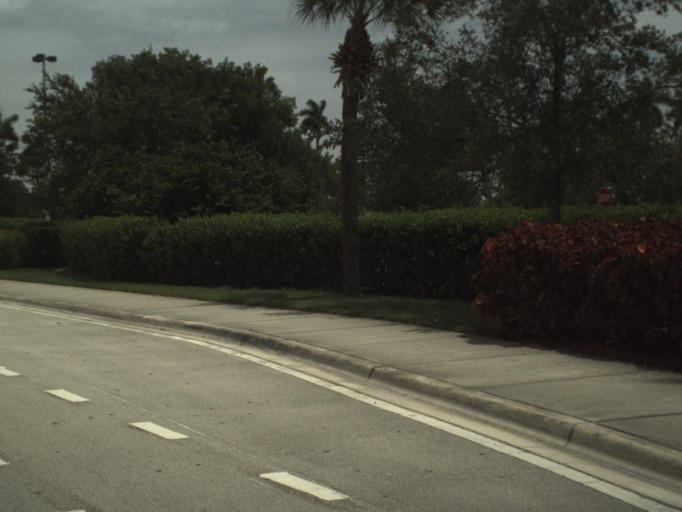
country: US
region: Florida
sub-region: Broward County
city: Hallandale Beach
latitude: 25.9808
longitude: -80.1420
